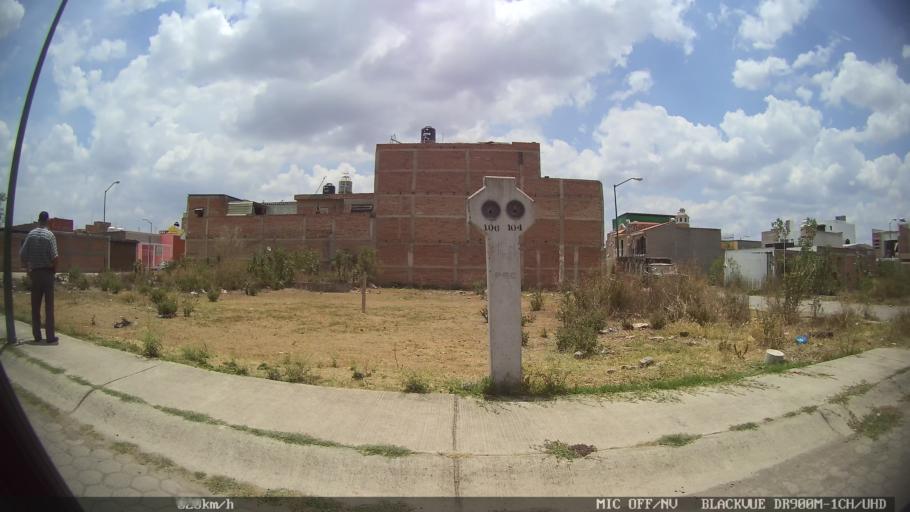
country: MX
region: Jalisco
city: Coyula
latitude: 20.6637
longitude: -103.2260
